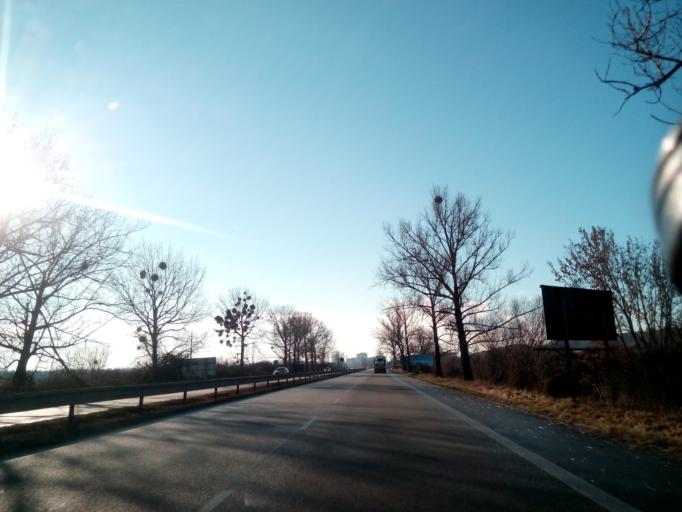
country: SK
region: Kosicky
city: Kosice
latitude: 48.6568
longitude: 21.2060
